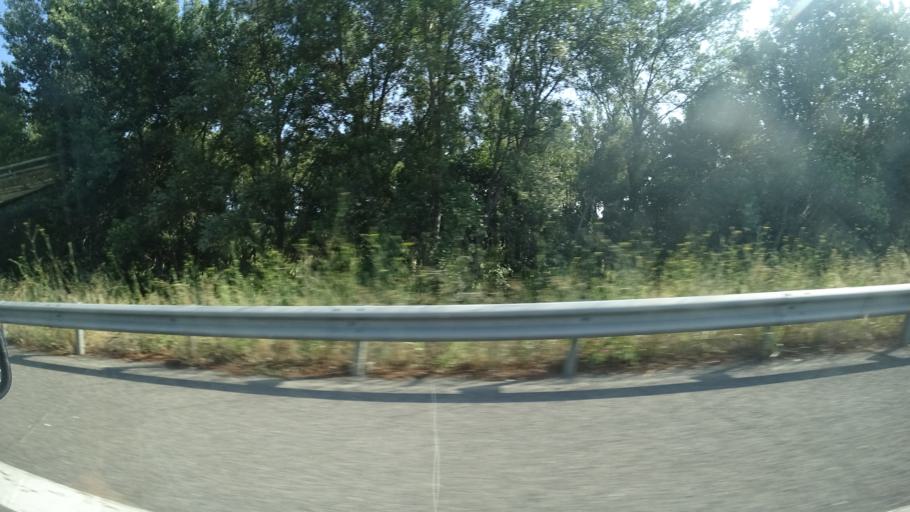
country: FR
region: Languedoc-Roussillon
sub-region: Departement des Pyrenees-Orientales
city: Millas
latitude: 42.6970
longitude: 2.6920
